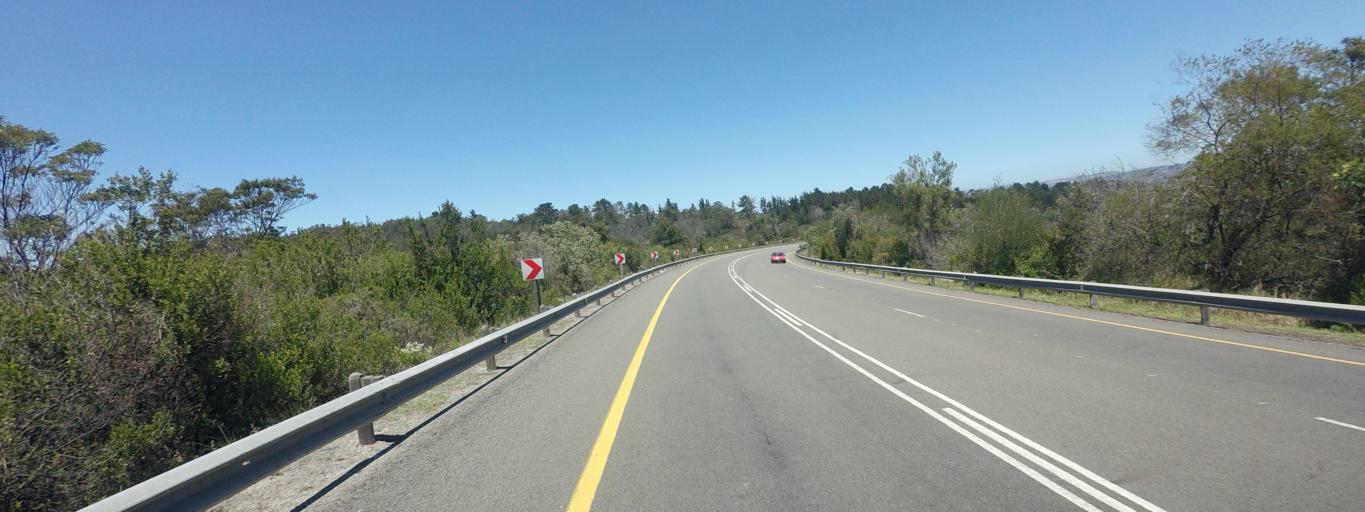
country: ZA
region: Western Cape
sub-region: Eden District Municipality
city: Plettenberg Bay
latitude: -33.9978
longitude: 23.4347
